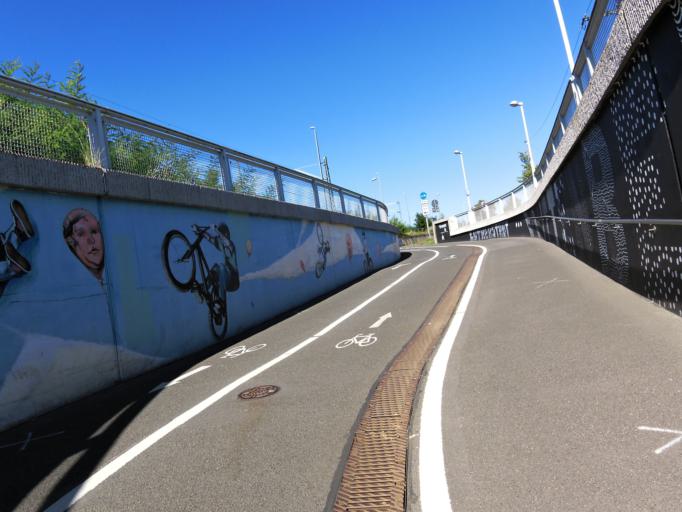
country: DE
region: Saxony-Anhalt
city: Wittenburg
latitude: 51.8633
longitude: 12.6569
